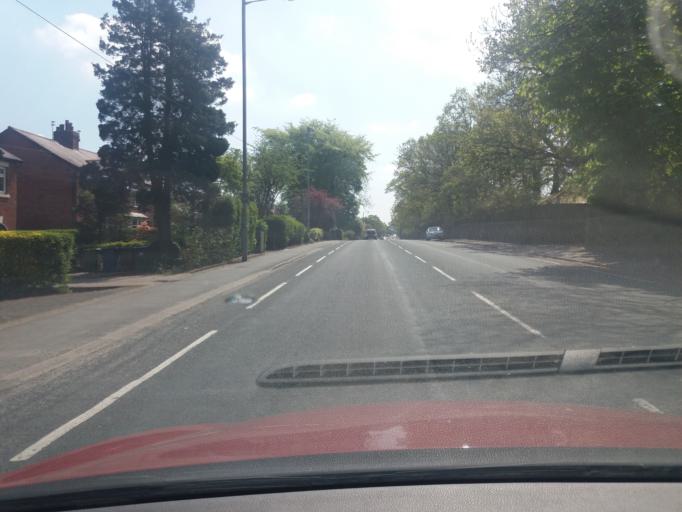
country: GB
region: England
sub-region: Lancashire
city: Clayton-le-Woods
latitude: 53.6809
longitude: -2.6371
